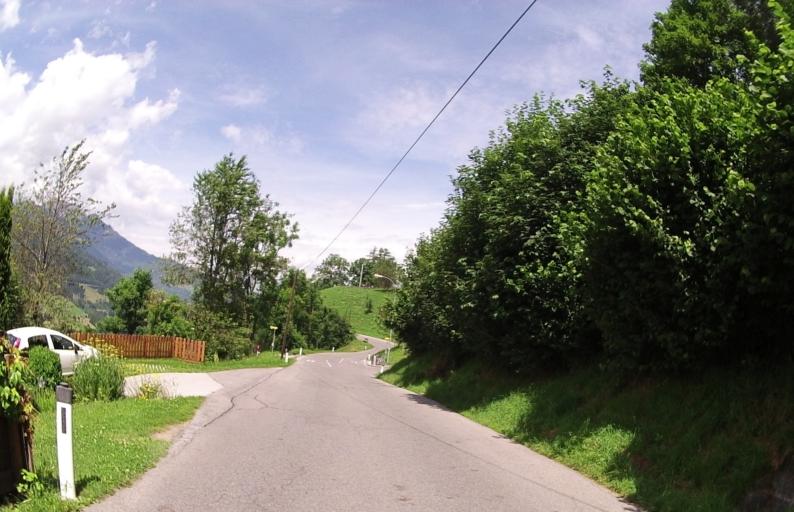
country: AT
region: Tyrol
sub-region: Politischer Bezirk Innsbruck Land
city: Ellbogen
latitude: 47.1702
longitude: 11.4430
